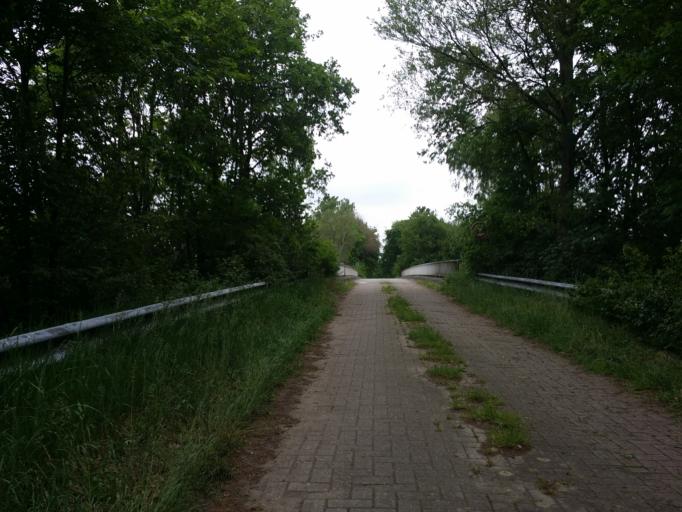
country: DE
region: Lower Saxony
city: Hude
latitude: 53.0586
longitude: 8.4441
